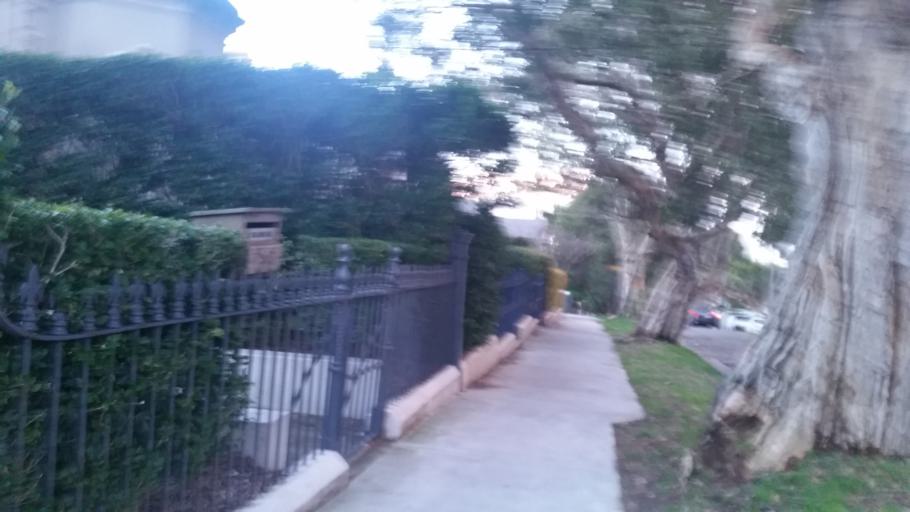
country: AU
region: New South Wales
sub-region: Waverley
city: Bronte
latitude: -33.9049
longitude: 151.2609
